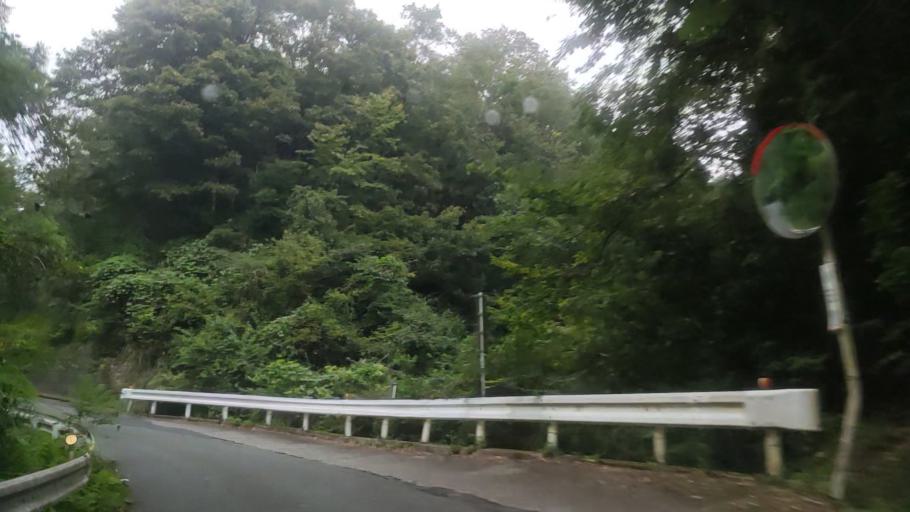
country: JP
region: Wakayama
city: Hashimoto
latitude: 34.2931
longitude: 135.6297
